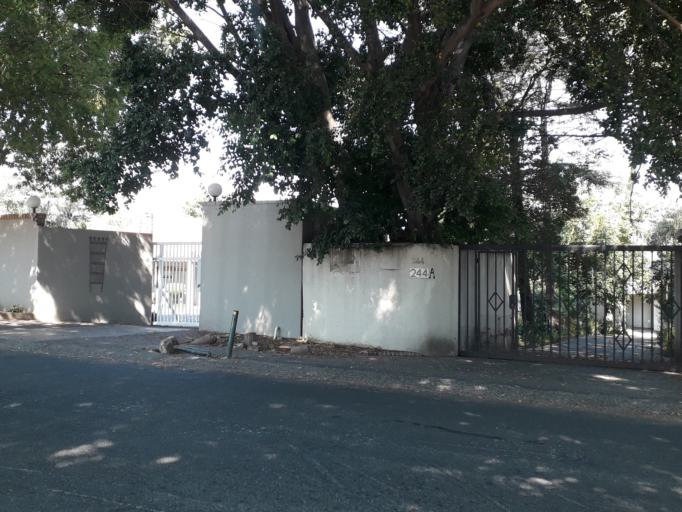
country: ZA
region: Gauteng
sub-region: City of Johannesburg Metropolitan Municipality
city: Johannesburg
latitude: -26.1013
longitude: 28.0008
